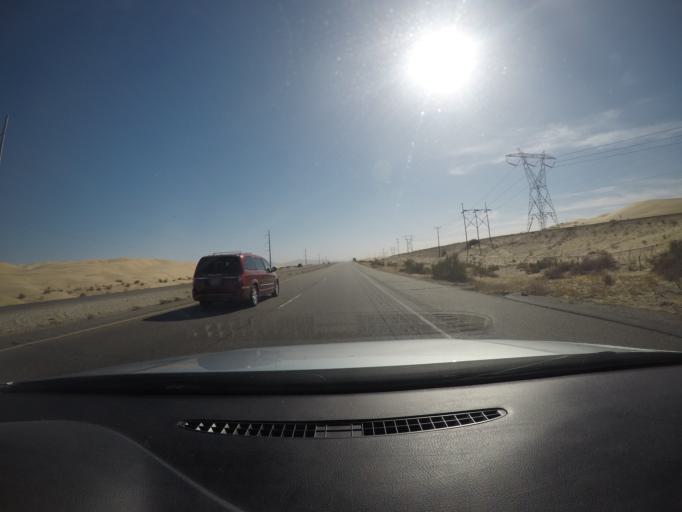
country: MX
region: Baja California
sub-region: Mexicali
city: Ejido Tabasco
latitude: 32.7308
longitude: -114.9051
